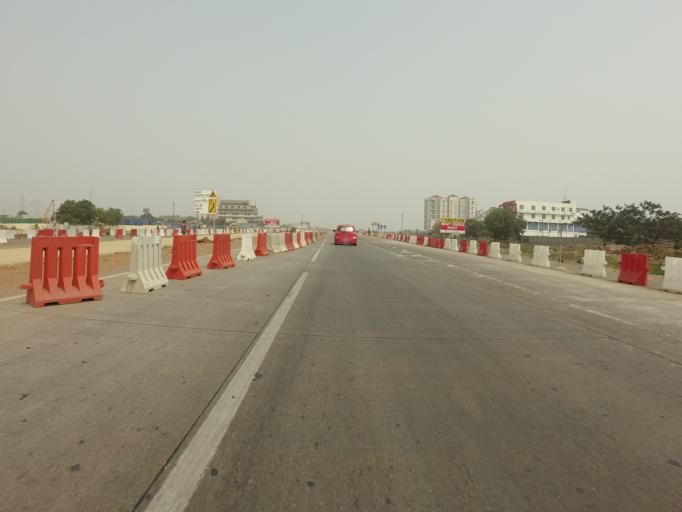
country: GH
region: Greater Accra
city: Tema
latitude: 5.6847
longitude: -0.0195
